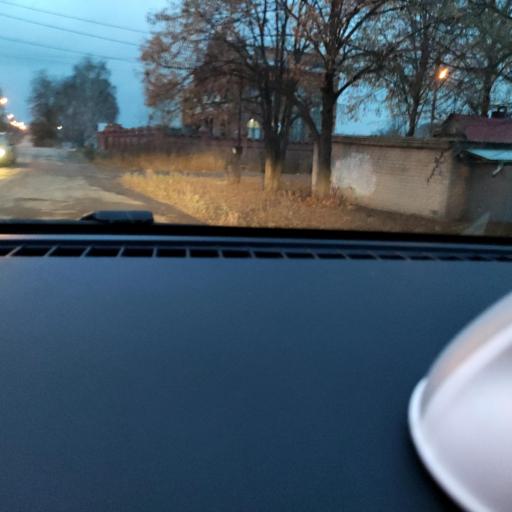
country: RU
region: Samara
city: Smyshlyayevka
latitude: 53.2530
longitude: 50.3484
